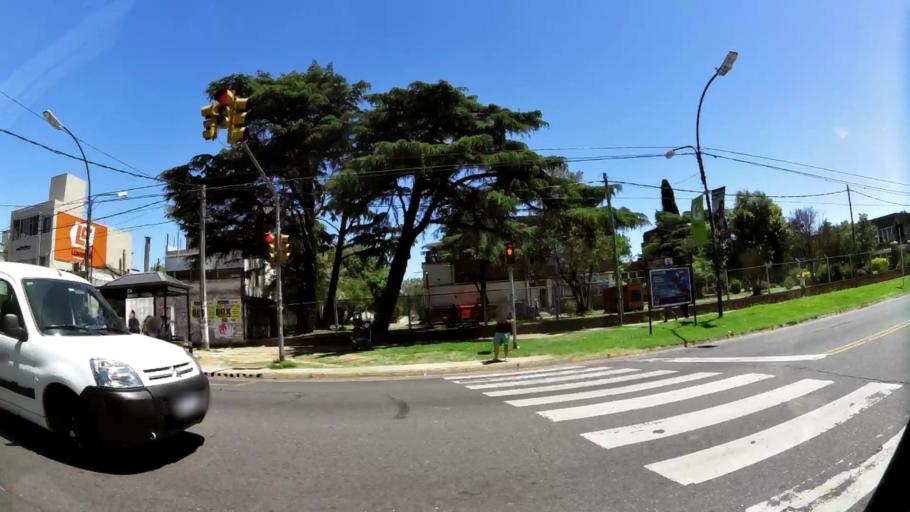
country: AR
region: Buenos Aires
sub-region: Partido de San Isidro
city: San Isidro
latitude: -34.4963
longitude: -58.5208
